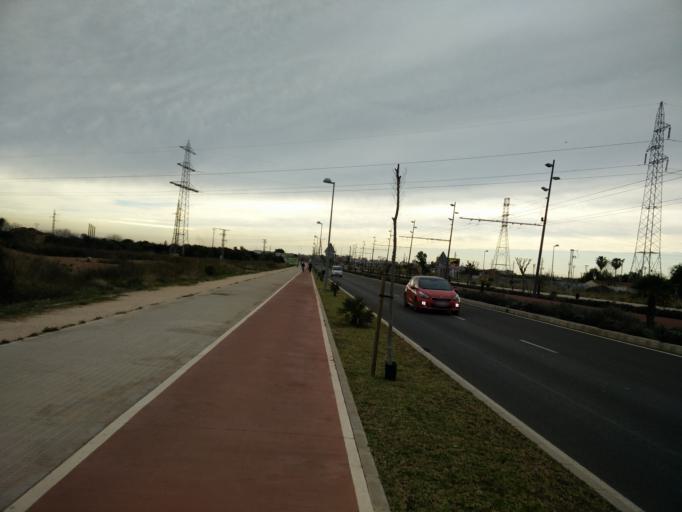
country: ES
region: Valencia
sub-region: Provincia de Castello
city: Castello de la Plana
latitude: 39.9820
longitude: -0.0153
